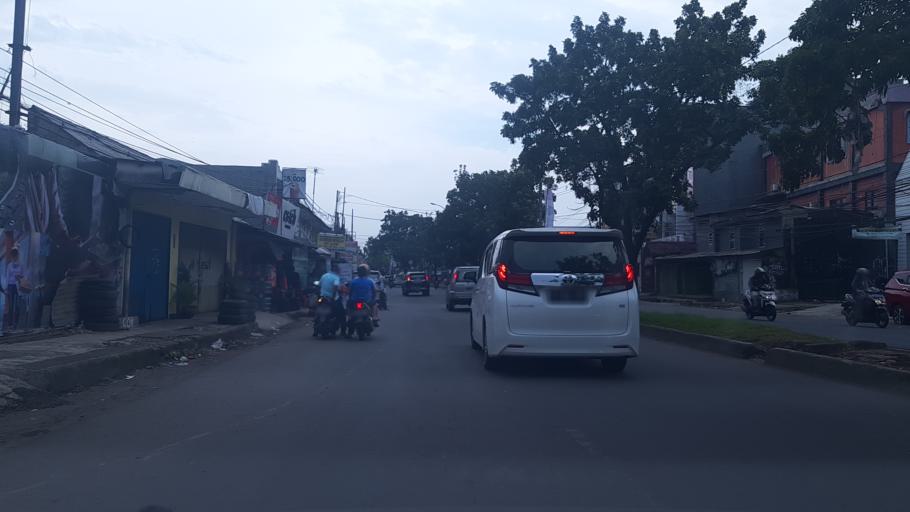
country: ID
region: West Java
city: Cibinong
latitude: -6.4751
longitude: 106.8635
